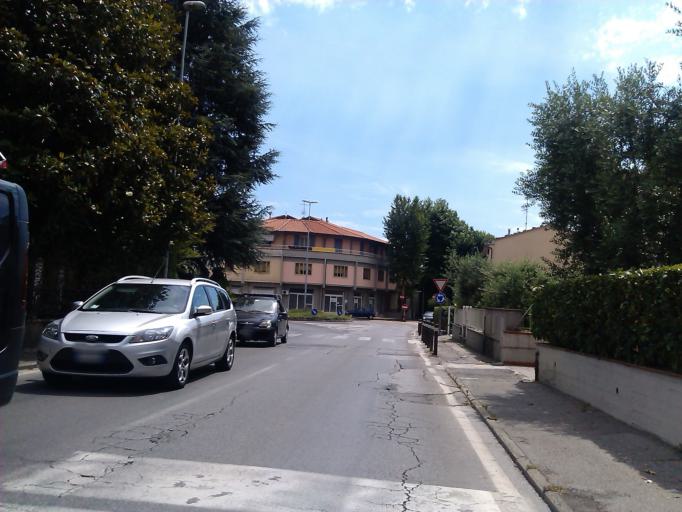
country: IT
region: Tuscany
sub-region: Provincia di Pistoia
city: Montale
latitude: 43.9370
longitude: 11.0258
